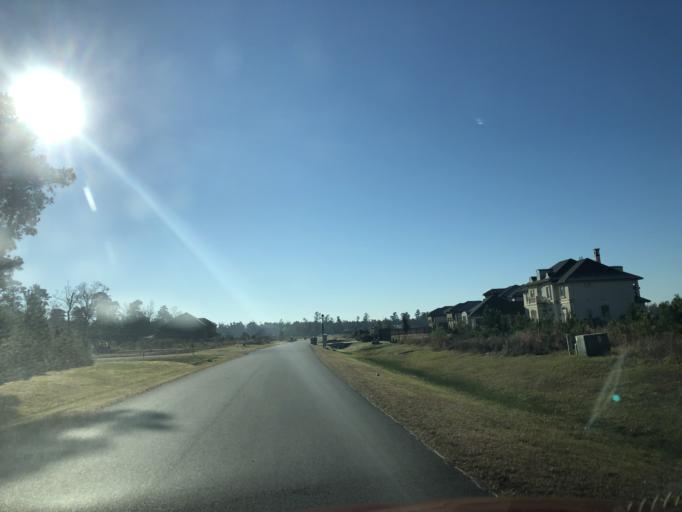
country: US
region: Texas
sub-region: Montgomery County
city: Porter Heights
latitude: 30.0773
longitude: -95.3198
